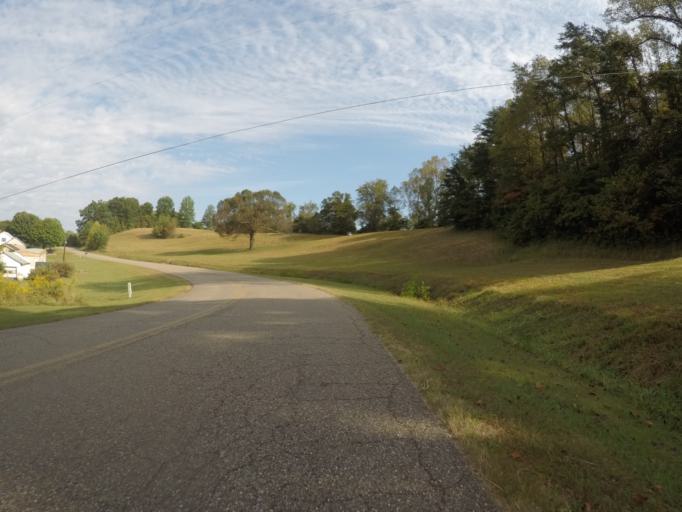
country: US
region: West Virginia
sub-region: Cabell County
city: Lesage
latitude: 38.5602
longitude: -82.4249
